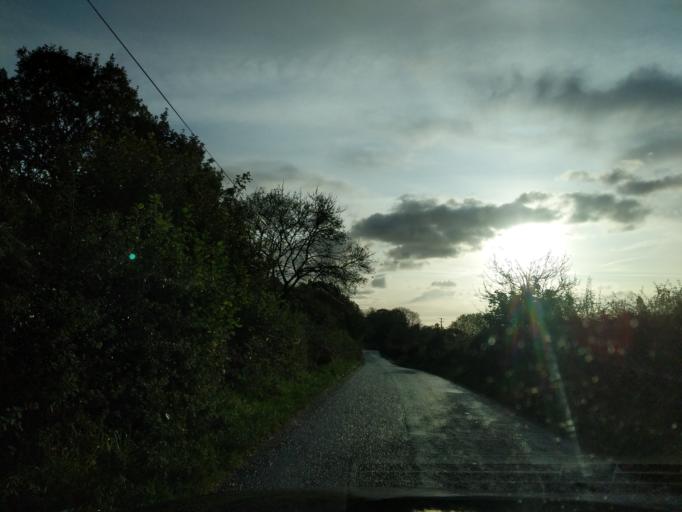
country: GB
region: Scotland
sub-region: Dumfries and Galloway
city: Kirkcudbright
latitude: 54.8247
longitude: -4.1982
